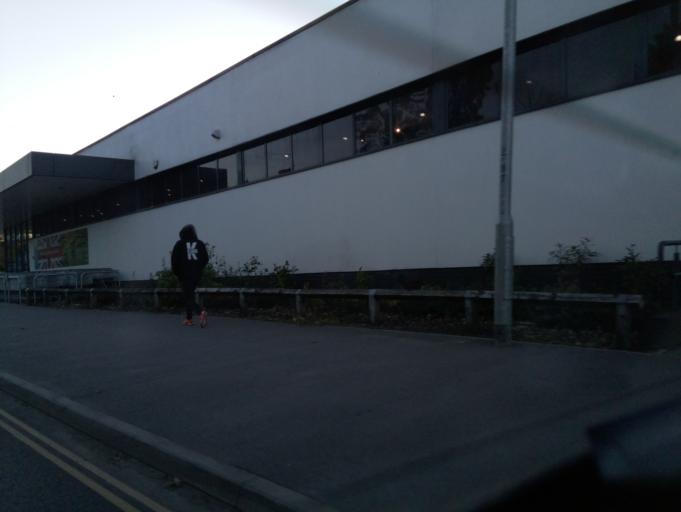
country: GB
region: England
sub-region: Wiltshire
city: Westbury
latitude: 51.2578
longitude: -2.1850
